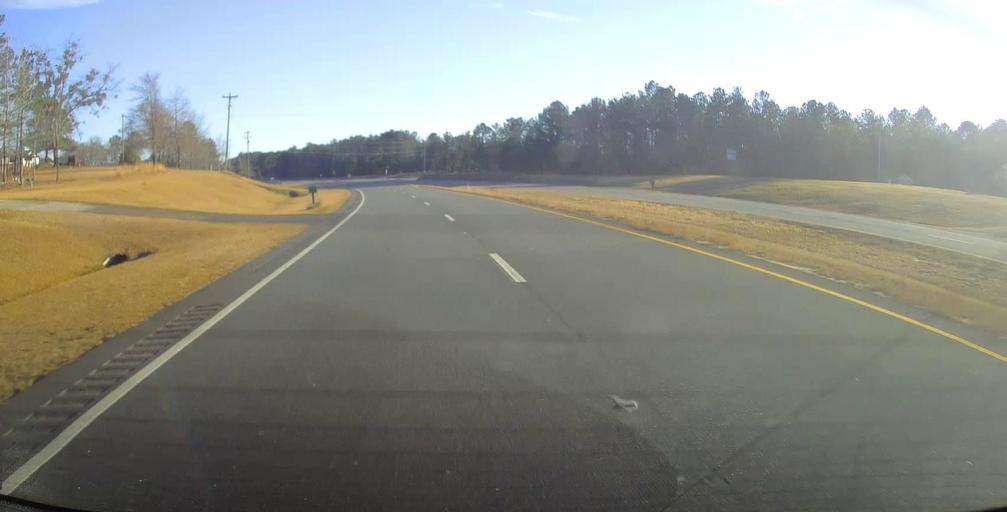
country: US
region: Georgia
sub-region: Upson County
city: Thomaston
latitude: 32.7717
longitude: -84.2486
